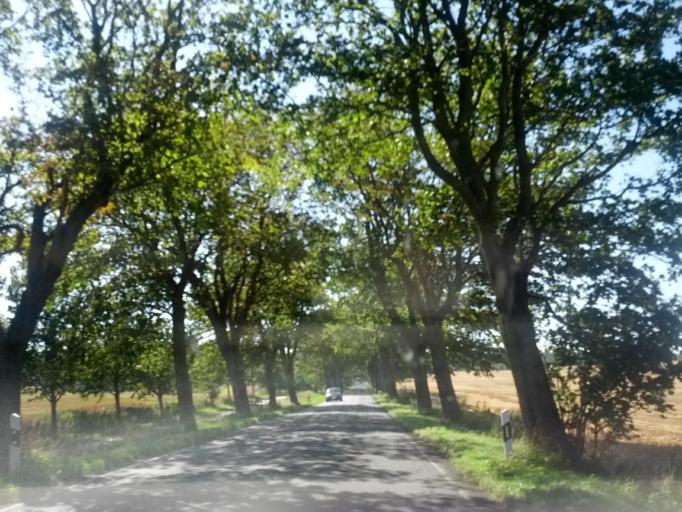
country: DE
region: Mecklenburg-Vorpommern
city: Bergen auf Ruegen
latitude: 54.4312
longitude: 13.4326
